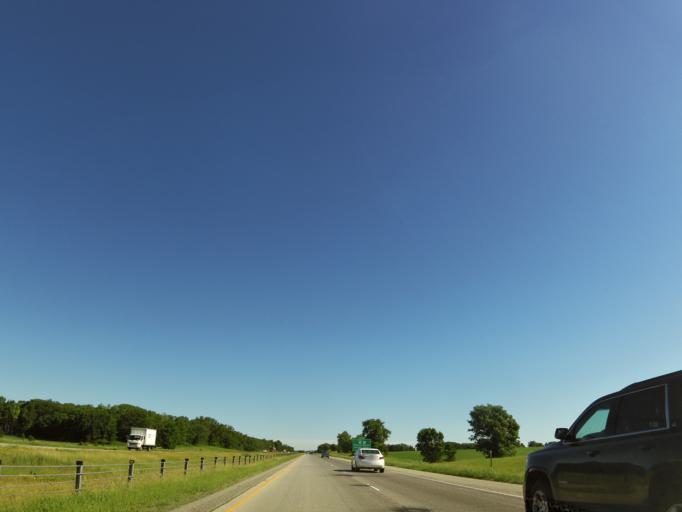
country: US
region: Minnesota
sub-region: Otter Tail County
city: Fergus Falls
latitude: 46.3176
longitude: -96.1225
